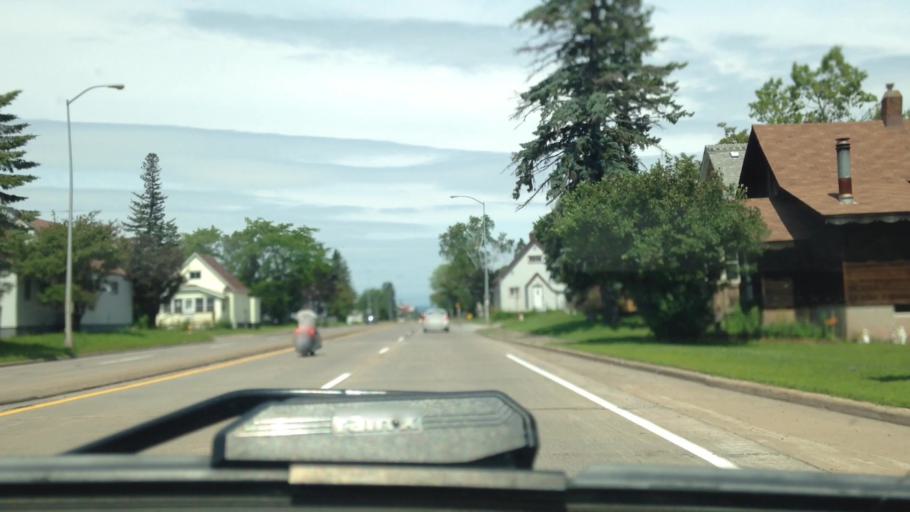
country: US
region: Wisconsin
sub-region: Douglas County
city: Superior
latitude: 46.6742
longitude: -92.0060
